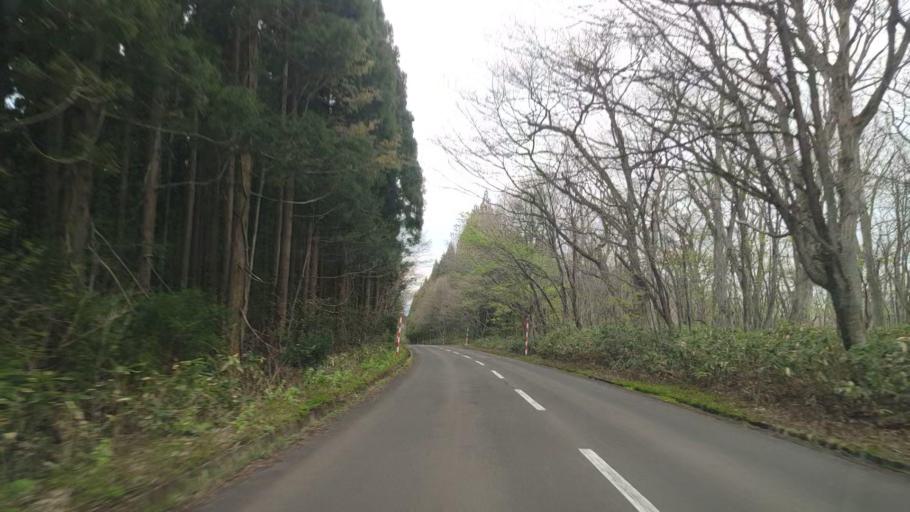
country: JP
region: Akita
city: Hanawa
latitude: 40.3883
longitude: 140.7935
